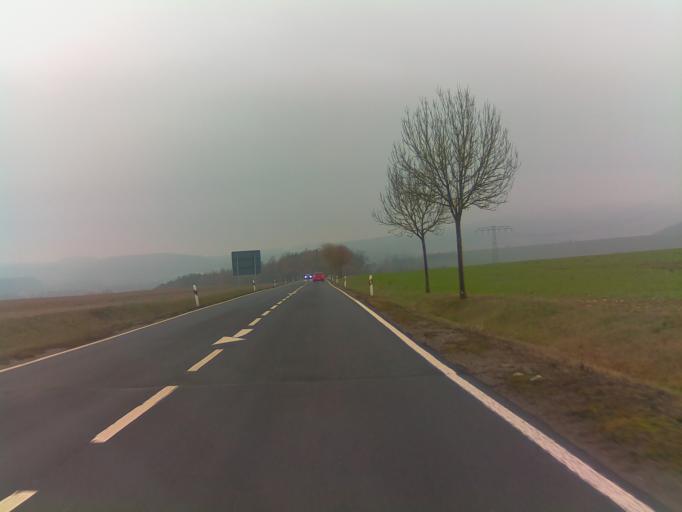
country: DE
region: Thuringia
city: Ehrenberg
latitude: 50.4806
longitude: 10.6496
